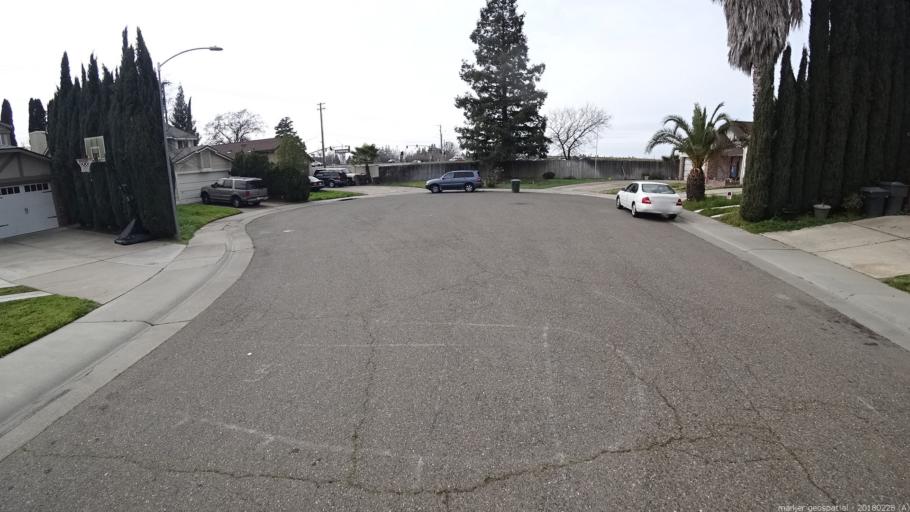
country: US
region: California
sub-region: Sacramento County
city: Antelope
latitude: 38.7042
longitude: -121.3444
